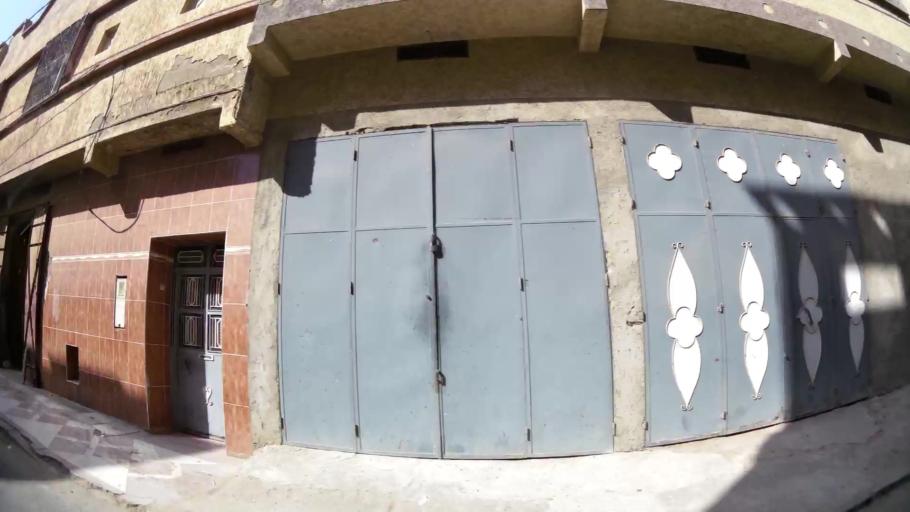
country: MA
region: Oriental
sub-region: Oujda-Angad
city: Oujda
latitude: 34.7121
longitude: -1.8860
